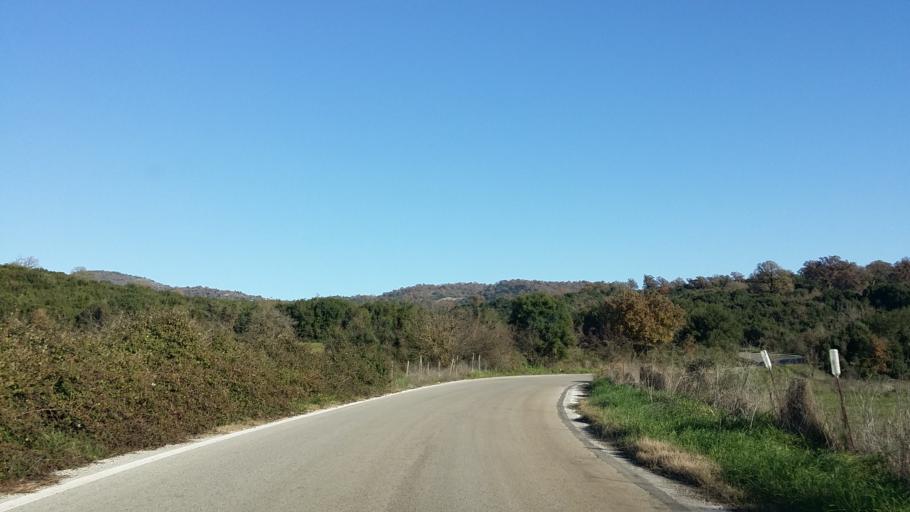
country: GR
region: West Greece
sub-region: Nomos Aitolias kai Akarnanias
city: Fitiai
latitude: 38.6344
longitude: 21.1628
